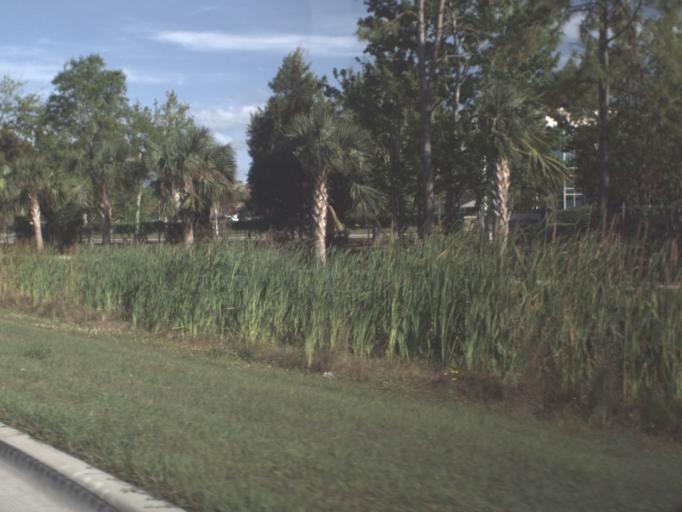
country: US
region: Florida
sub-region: Flagler County
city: Palm Coast
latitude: 29.5533
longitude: -81.2250
